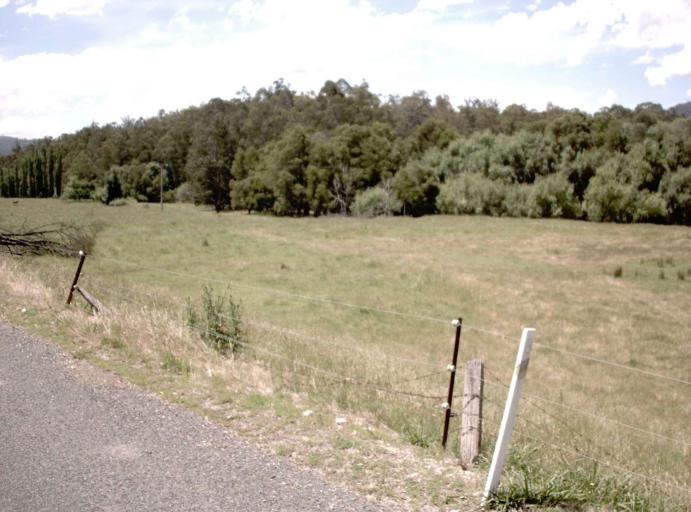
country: AU
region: New South Wales
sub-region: Bombala
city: Bombala
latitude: -37.3868
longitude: 149.0131
